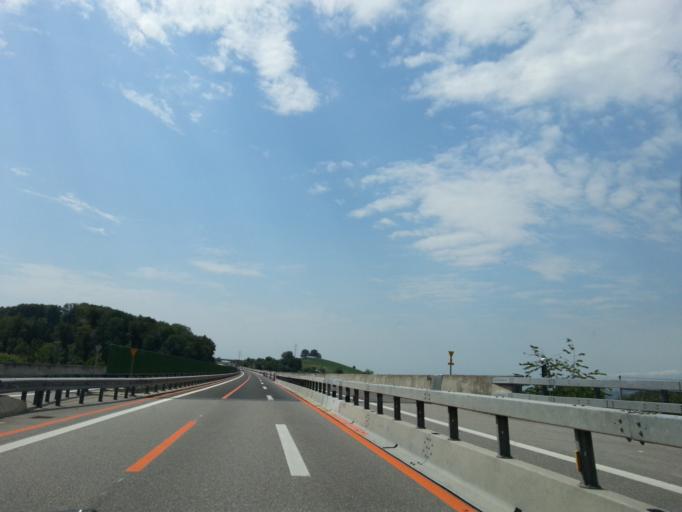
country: CH
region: Fribourg
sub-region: See District
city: Murten
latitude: 46.9398
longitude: 7.1480
